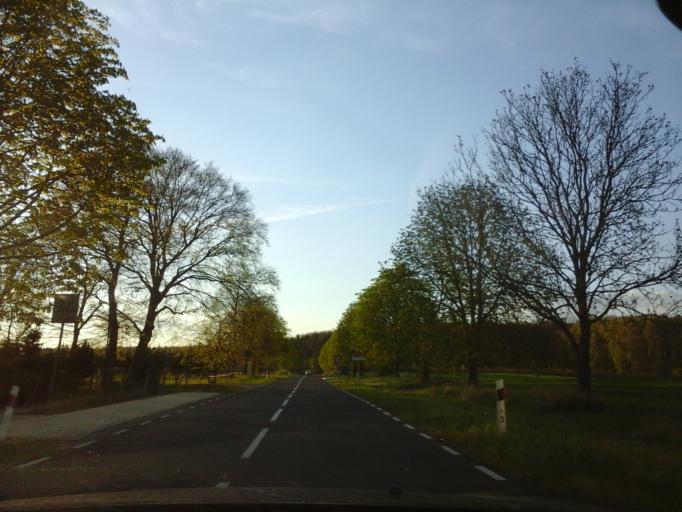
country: PL
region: West Pomeranian Voivodeship
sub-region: Powiat choszczenski
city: Bierzwnik
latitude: 53.0656
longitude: 15.6605
